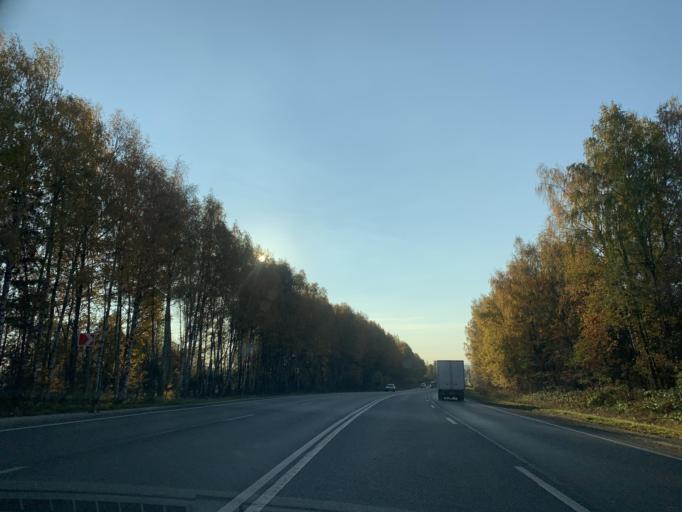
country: RU
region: Jaroslavl
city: Konstantinovskiy
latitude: 57.7737
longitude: 39.6653
